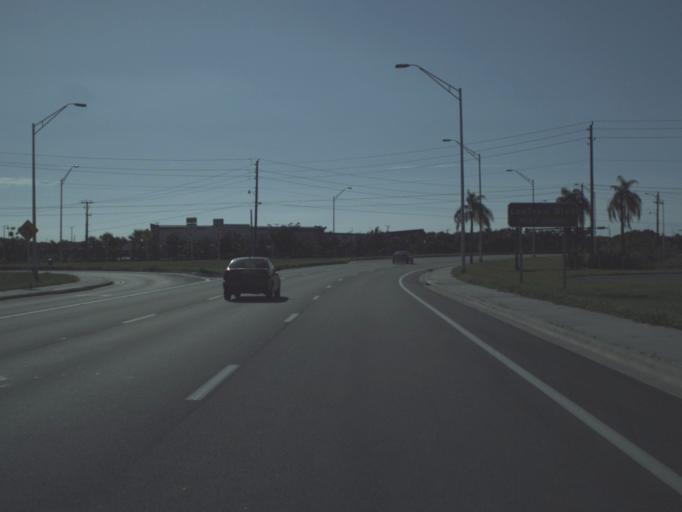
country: US
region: Florida
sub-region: Lee County
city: Fort Myers
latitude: 26.6197
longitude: -81.8611
